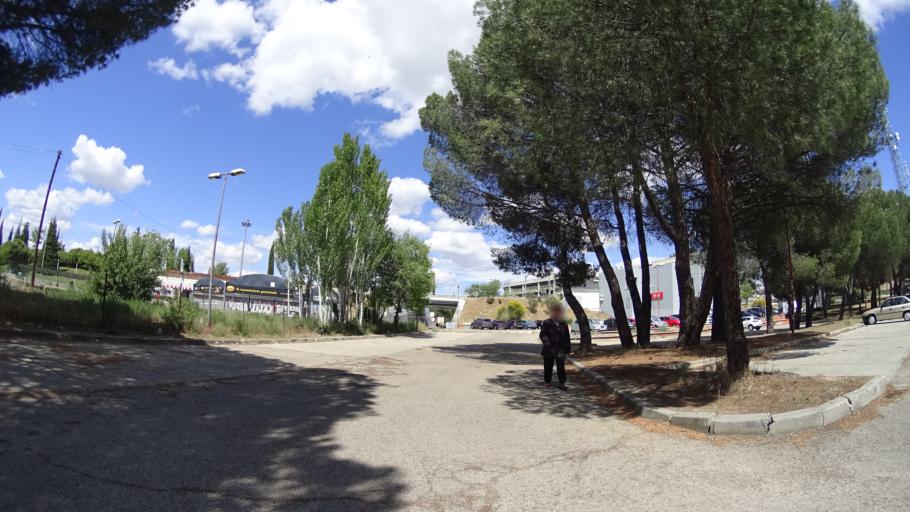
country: ES
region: Madrid
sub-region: Provincia de Madrid
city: Majadahonda
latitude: 40.4742
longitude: -3.8473
